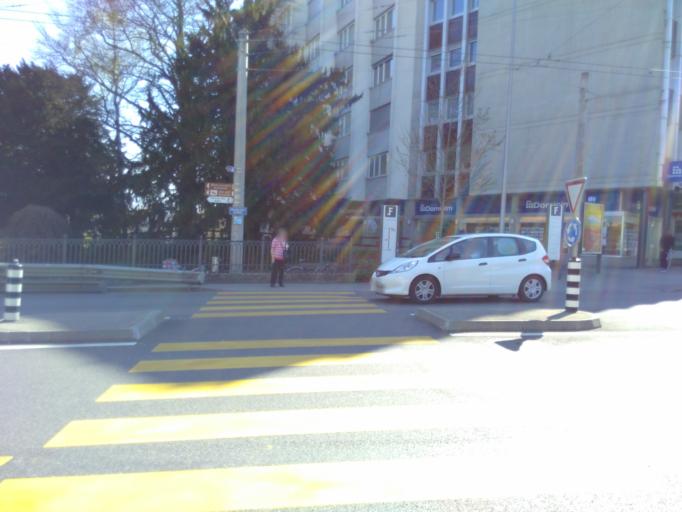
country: CH
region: Fribourg
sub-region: Sarine District
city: Fribourg
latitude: 46.8043
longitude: 7.1563
